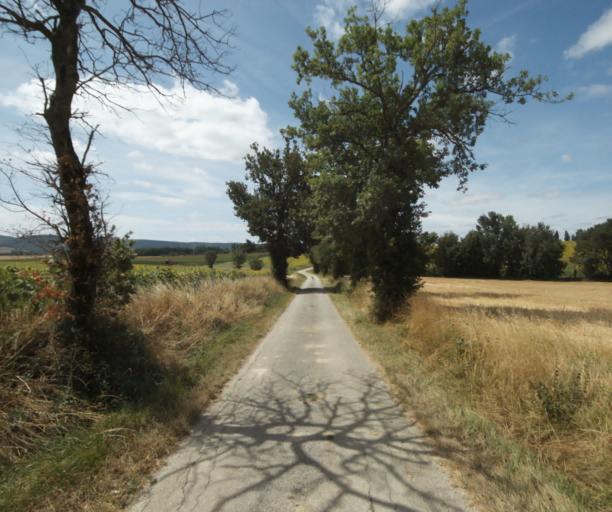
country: FR
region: Midi-Pyrenees
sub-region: Departement du Tarn
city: Soreze
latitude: 43.4863
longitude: 2.0704
